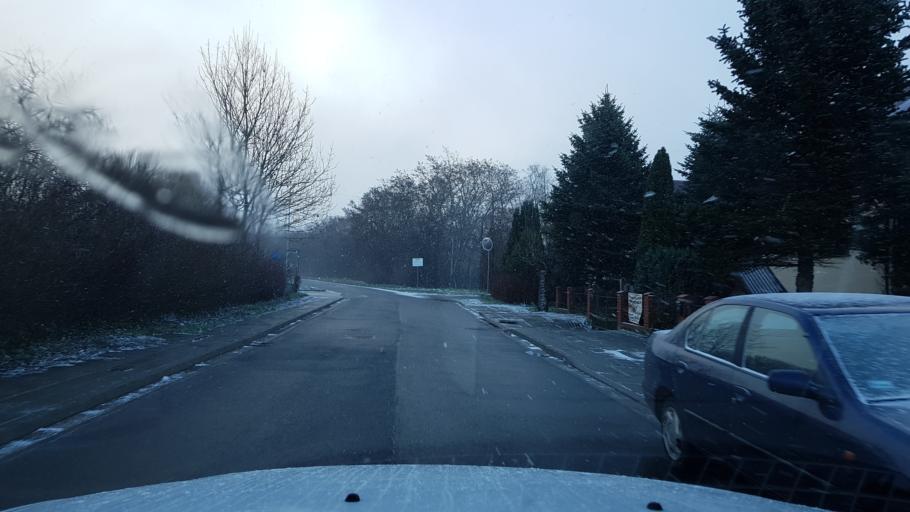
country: PL
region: West Pomeranian Voivodeship
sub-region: Powiat gryficki
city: Trzebiatow
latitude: 54.0570
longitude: 15.2866
